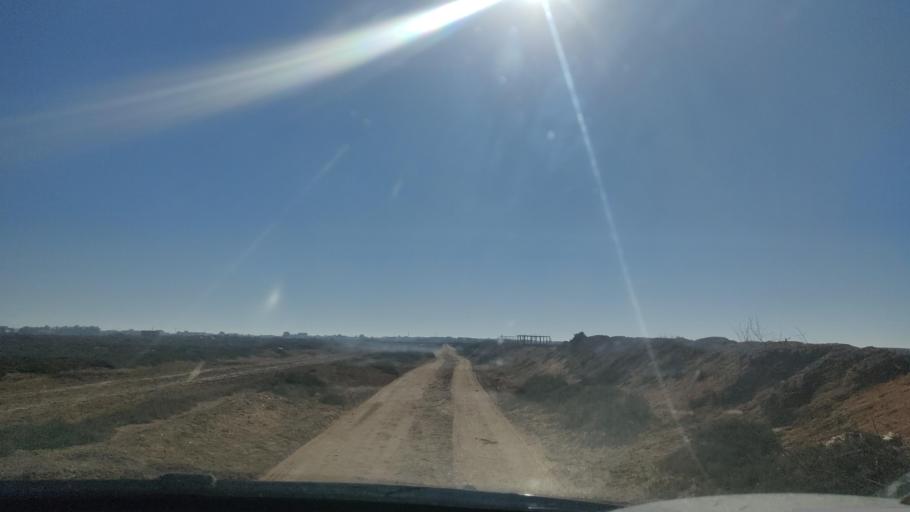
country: TN
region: Safaqis
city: Al Qarmadah
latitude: 34.8156
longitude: 10.8560
